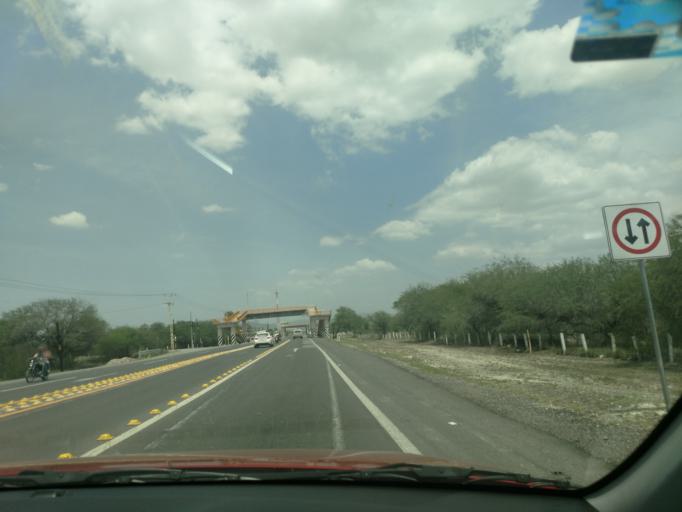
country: MX
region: San Luis Potosi
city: Rio Verde
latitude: 21.9196
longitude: -99.9556
